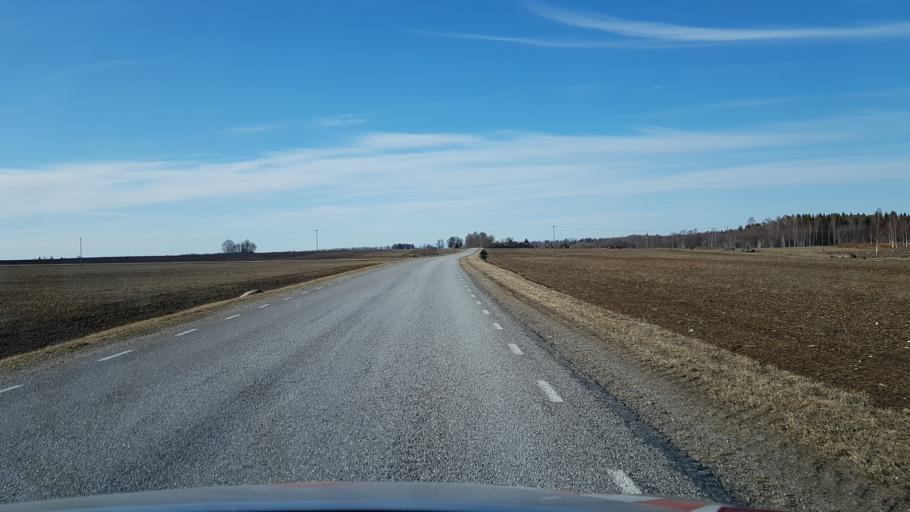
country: EE
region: Laeaene-Virumaa
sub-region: Kadrina vald
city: Kadrina
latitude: 59.3178
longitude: 26.1477
